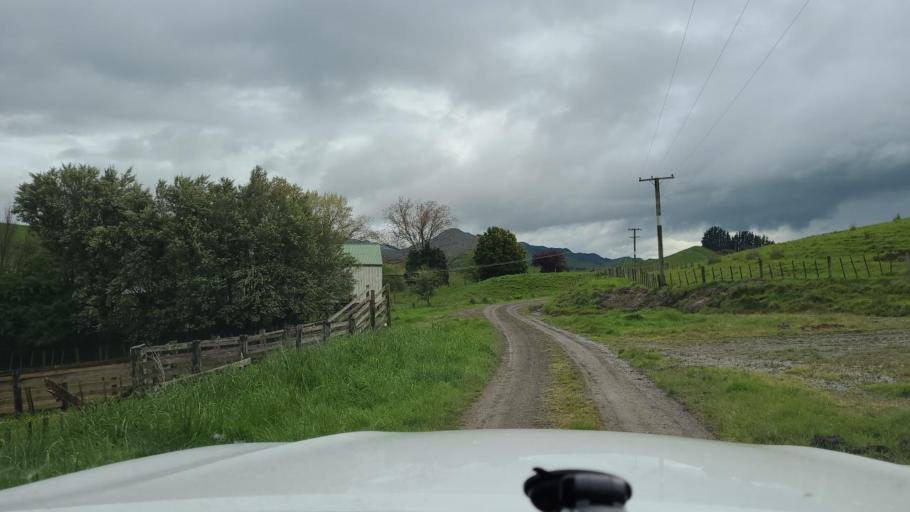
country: NZ
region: Gisborne
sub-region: Gisborne District
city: Gisborne
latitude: -38.4398
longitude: 177.6993
